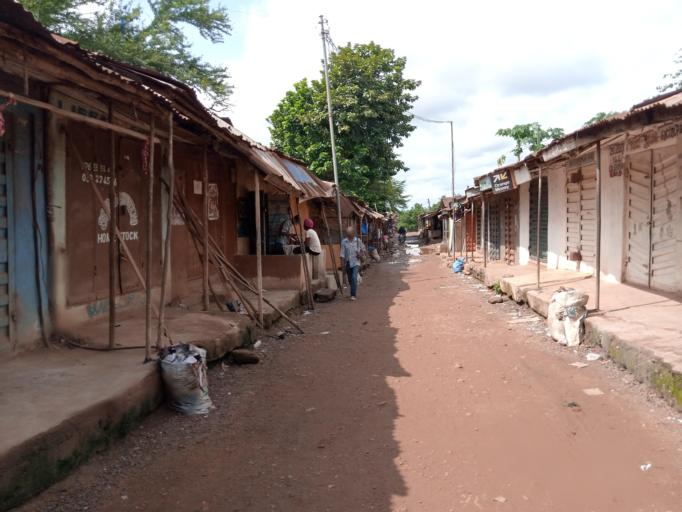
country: SL
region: Southern Province
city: Bo
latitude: 7.9631
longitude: -11.7357
